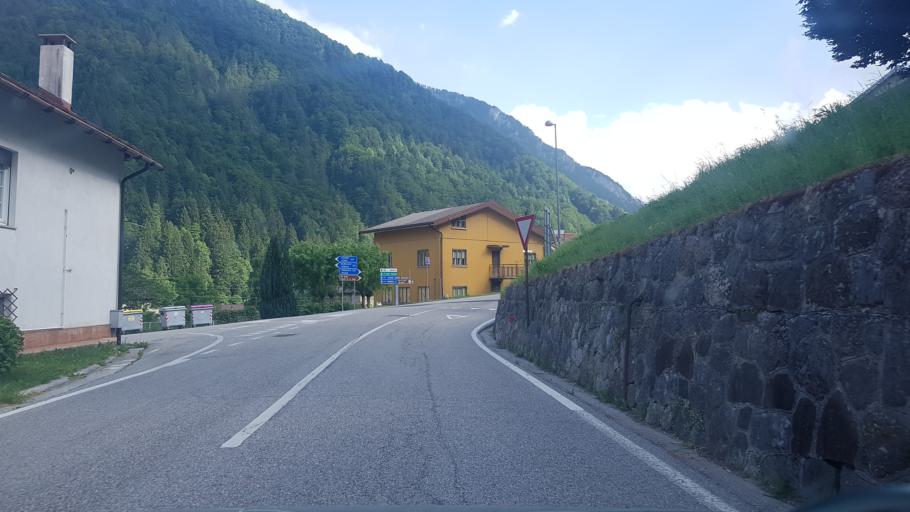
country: IT
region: Friuli Venezia Giulia
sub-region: Provincia di Udine
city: Pontebba
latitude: 46.5056
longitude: 13.3029
